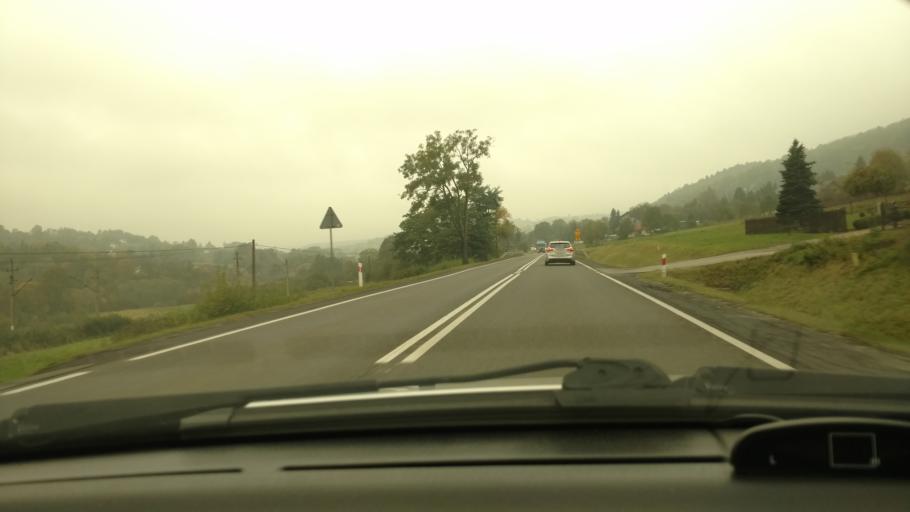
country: PL
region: Lesser Poland Voivodeship
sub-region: Powiat nowosadecki
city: Grybow
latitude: 49.6233
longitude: 20.9283
